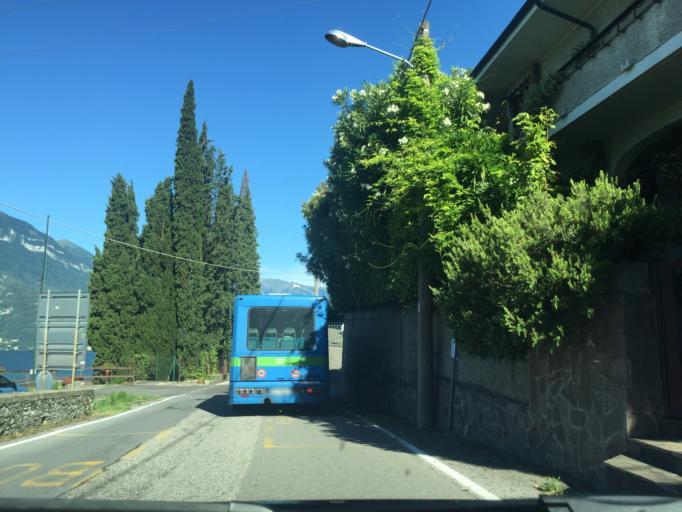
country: IT
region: Lombardy
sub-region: Provincia di Lecco
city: Perledo
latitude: 46.0152
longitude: 9.2931
